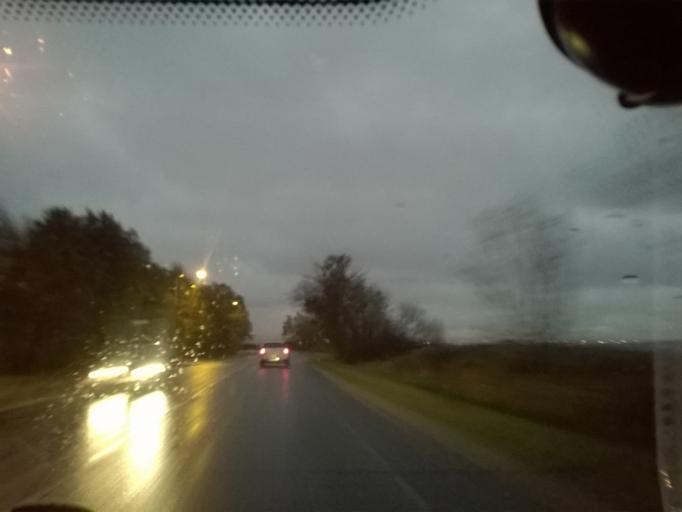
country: EE
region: Harju
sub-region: Viimsi vald
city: Rummu
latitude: 59.5351
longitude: 24.7931
